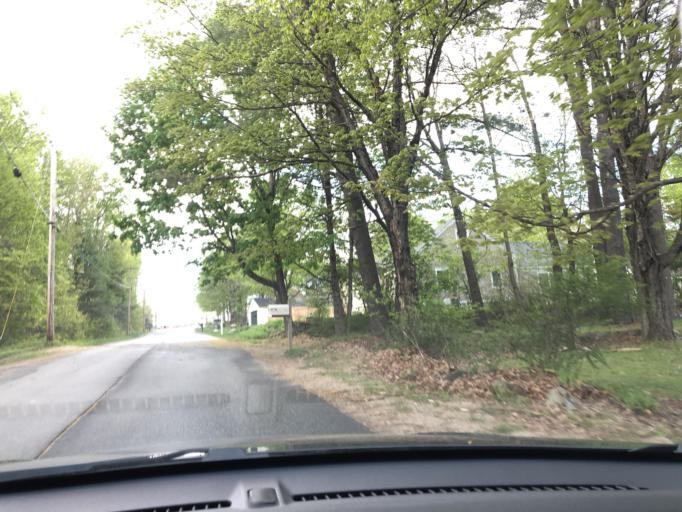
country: US
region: New Hampshire
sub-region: Merrimack County
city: New London
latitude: 43.4094
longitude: -71.9781
